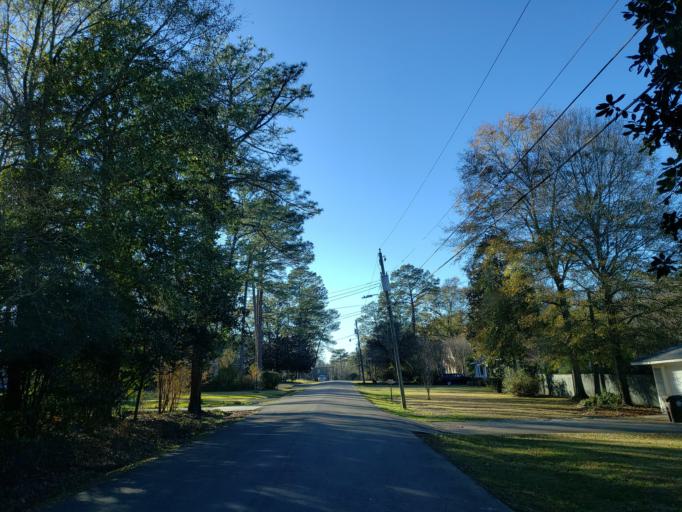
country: US
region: Mississippi
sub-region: Forrest County
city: Hattiesburg
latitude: 31.3156
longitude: -89.3166
